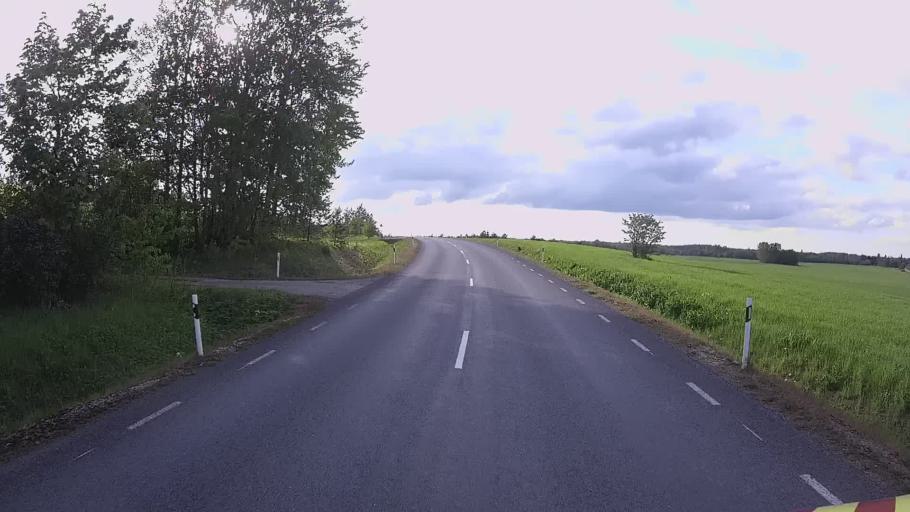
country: EE
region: Jogevamaa
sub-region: Mustvee linn
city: Mustvee
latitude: 59.0439
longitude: 27.0554
